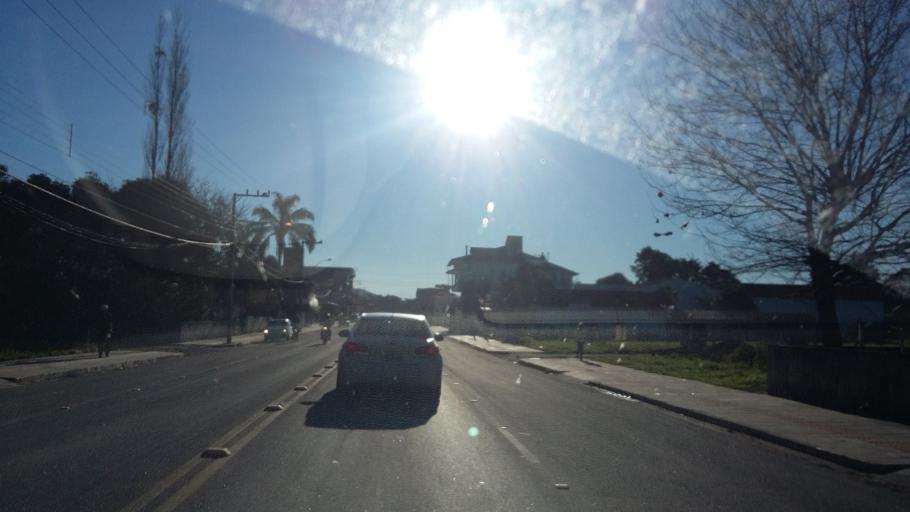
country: BR
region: Santa Catarina
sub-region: Lauro Muller
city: Lauro Muller
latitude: -27.9912
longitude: -49.5801
